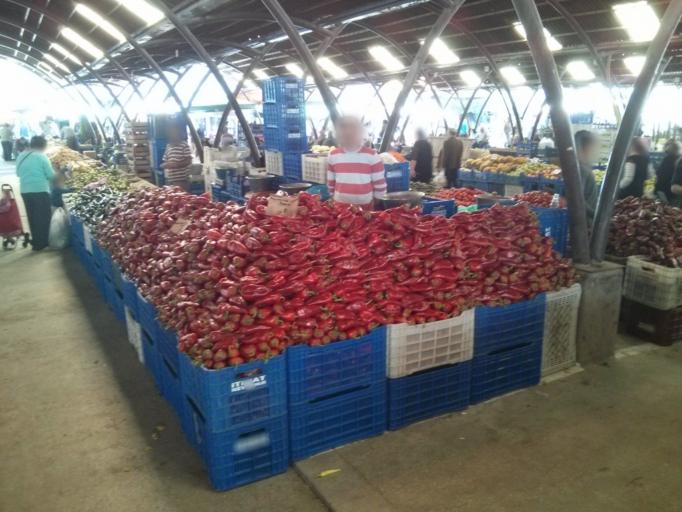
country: TR
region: Nevsehir
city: Avanos
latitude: 38.7143
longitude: 34.8451
